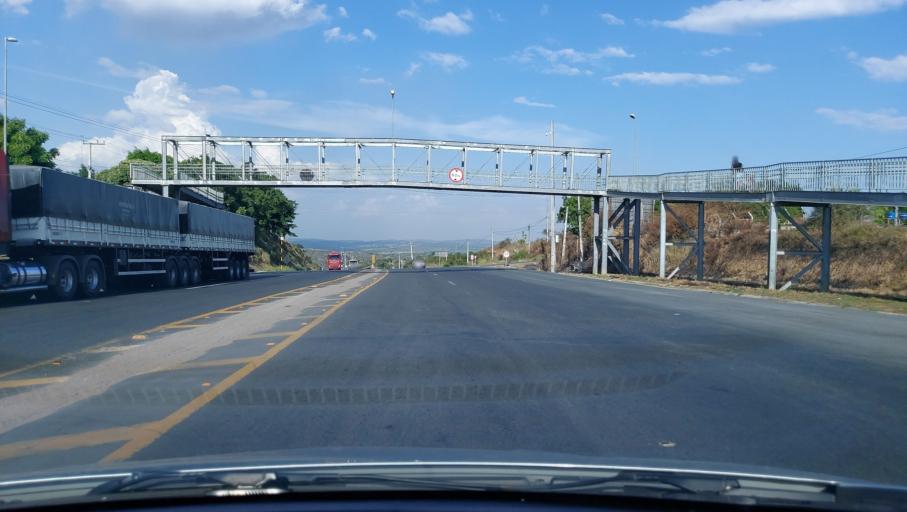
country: BR
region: Bahia
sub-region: Santo Estevao
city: Santo Estevao
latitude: -12.4390
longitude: -39.2272
